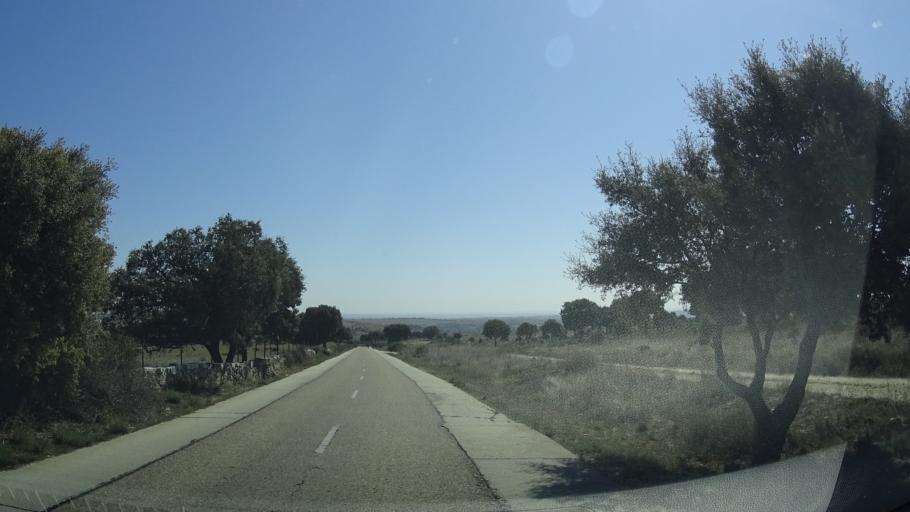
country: ES
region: Madrid
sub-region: Provincia de Madrid
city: Colmenar Viejo
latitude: 40.6447
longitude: -3.8196
